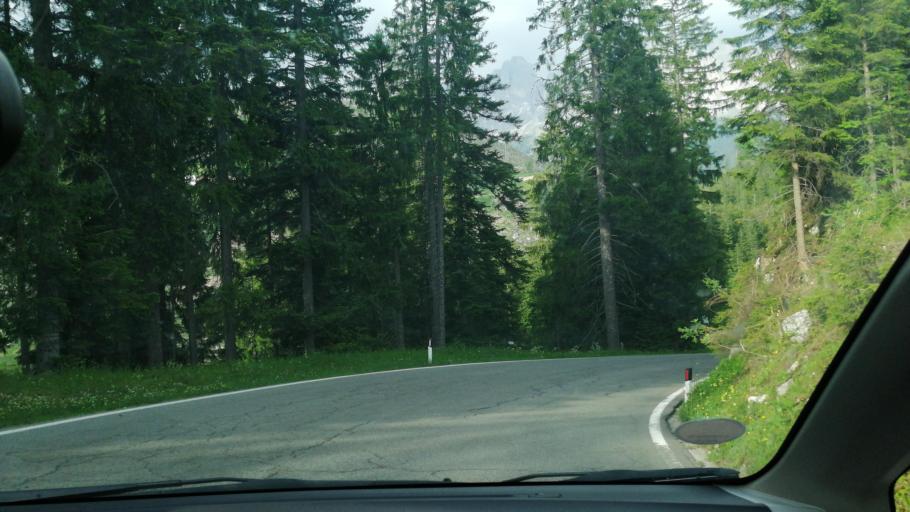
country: IT
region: Trentino-Alto Adige
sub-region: Bolzano
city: Nova Levante
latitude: 46.4146
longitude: 11.5645
